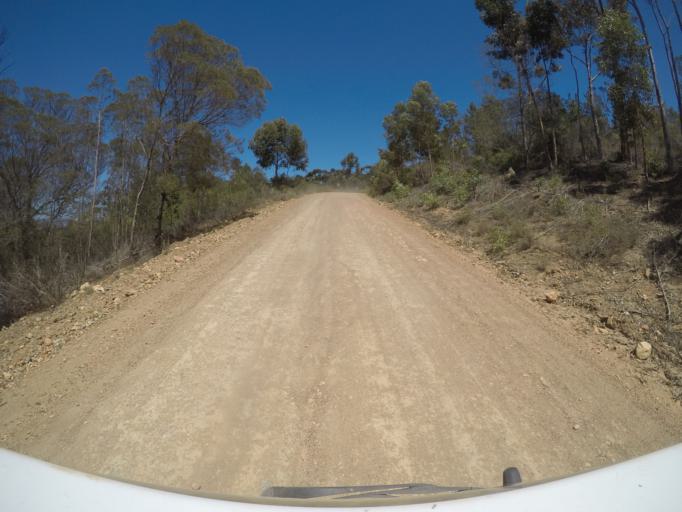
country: ZA
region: Western Cape
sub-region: Overberg District Municipality
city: Caledon
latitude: -34.1581
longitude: 19.2286
